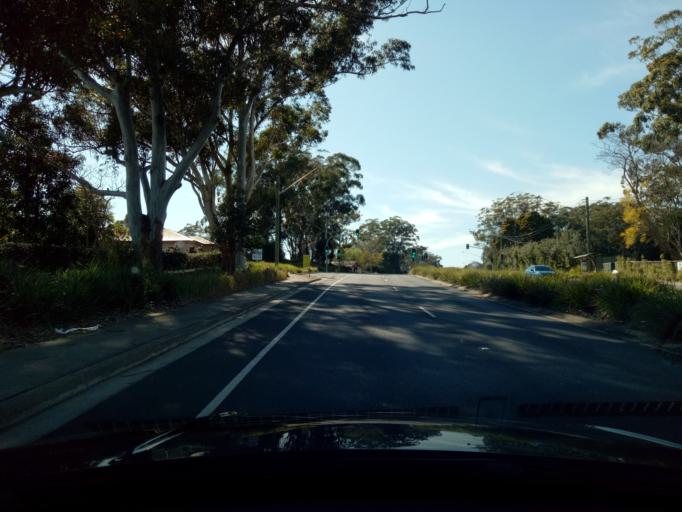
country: AU
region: New South Wales
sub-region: Gosford Shire
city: Erina
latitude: -33.4250
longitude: 151.4042
